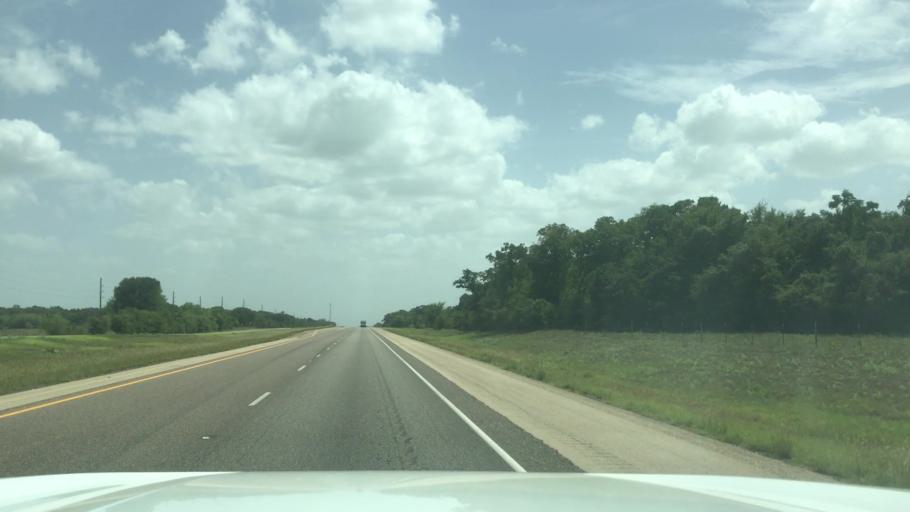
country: US
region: Texas
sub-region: Robertson County
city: Calvert
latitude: 31.0504
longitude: -96.7112
